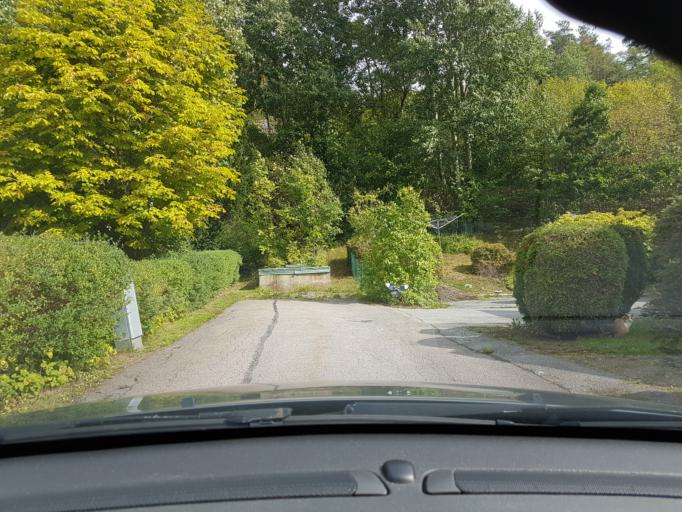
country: SE
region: Vaestra Goetaland
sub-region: Ale Kommun
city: Alafors
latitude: 57.9162
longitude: 12.0703
